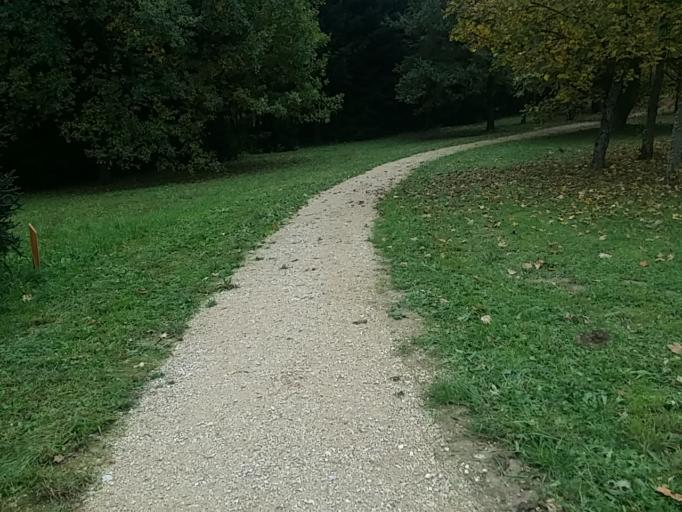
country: HU
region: Somogy
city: Kaposvar
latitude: 46.4464
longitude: 17.7901
